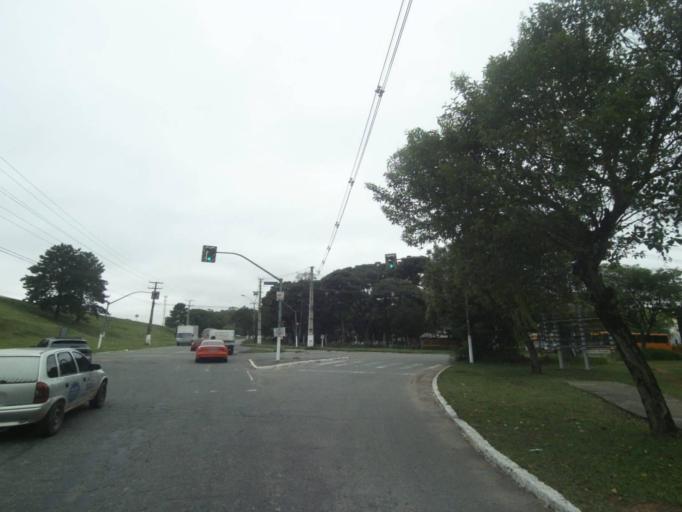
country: BR
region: Parana
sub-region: Sao Jose Dos Pinhais
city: Sao Jose dos Pinhais
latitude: -25.5349
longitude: -49.3175
